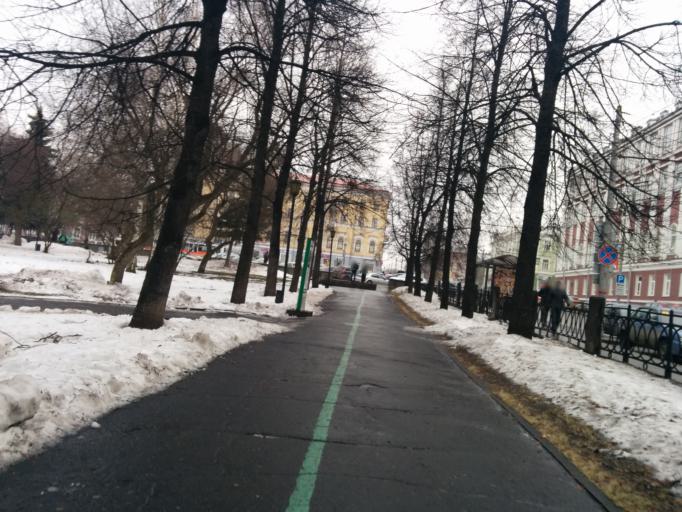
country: RU
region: Perm
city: Perm
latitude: 58.0144
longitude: 56.2458
